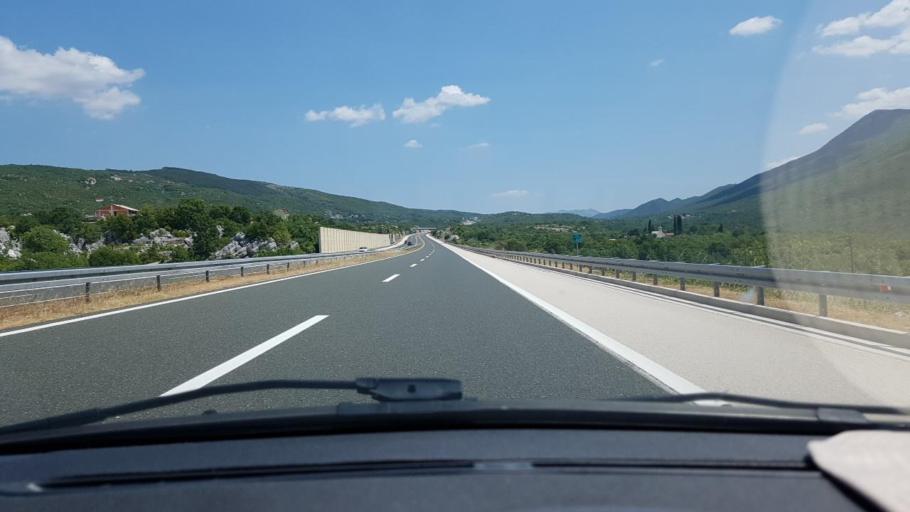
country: HR
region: Splitsko-Dalmatinska
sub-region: Grad Makarska
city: Makarska
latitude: 43.3918
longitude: 17.0504
